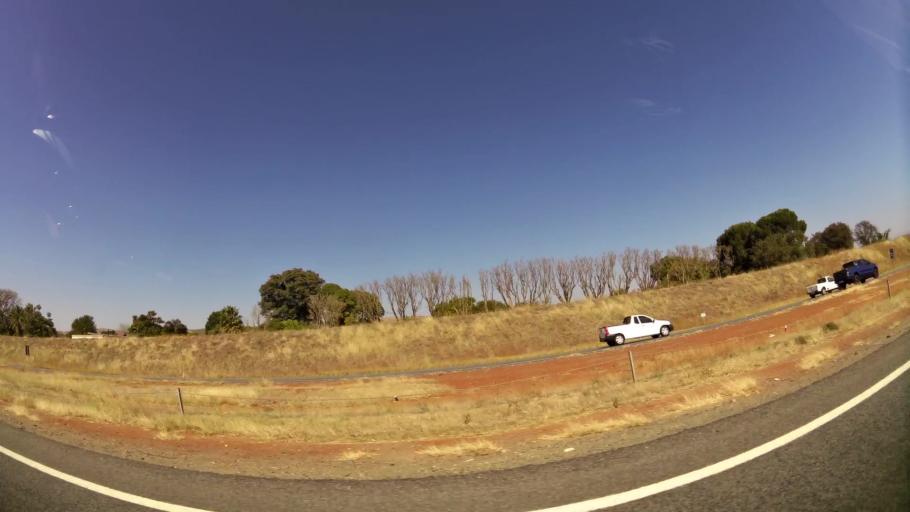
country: ZA
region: North-West
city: Ga-Rankuwa
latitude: -25.6563
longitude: 28.0538
